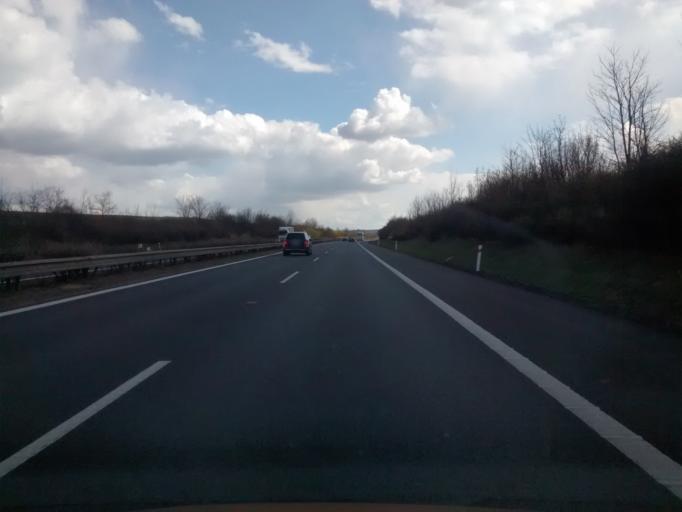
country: CZ
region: Central Bohemia
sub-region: Okres Melnik
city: Veltrusy
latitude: 50.2671
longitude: 14.3635
